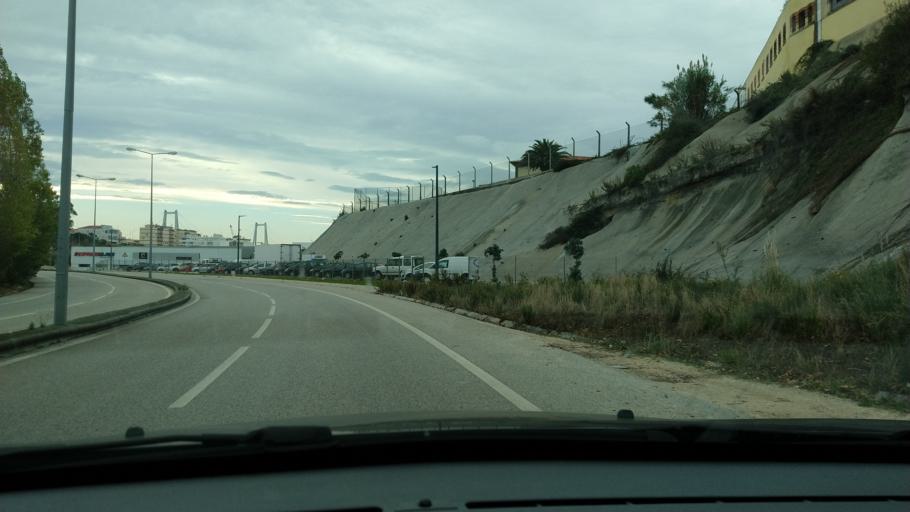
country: PT
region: Coimbra
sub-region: Figueira da Foz
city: Figueira da Foz
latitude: 40.1539
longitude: -8.8493
